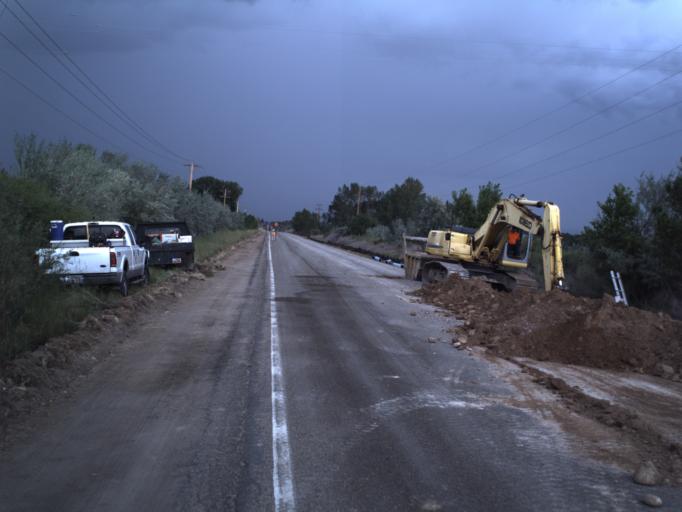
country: US
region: Utah
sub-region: Duchesne County
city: Roosevelt
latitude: 40.3927
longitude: -110.0298
